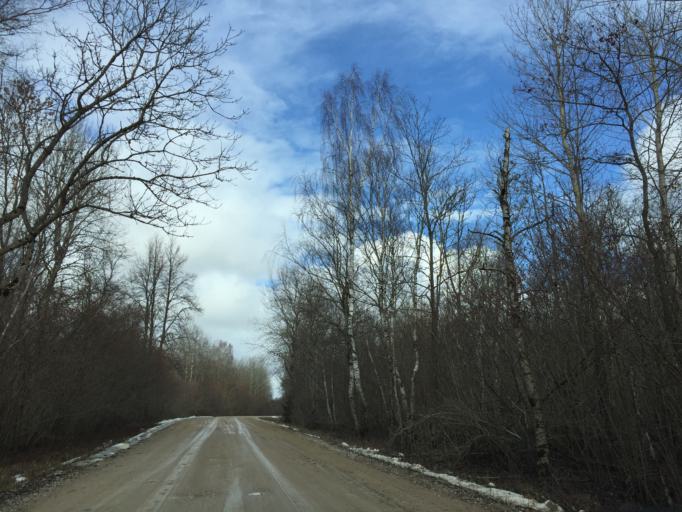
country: EE
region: Laeaene
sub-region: Lihula vald
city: Lihula
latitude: 58.7225
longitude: 23.8298
